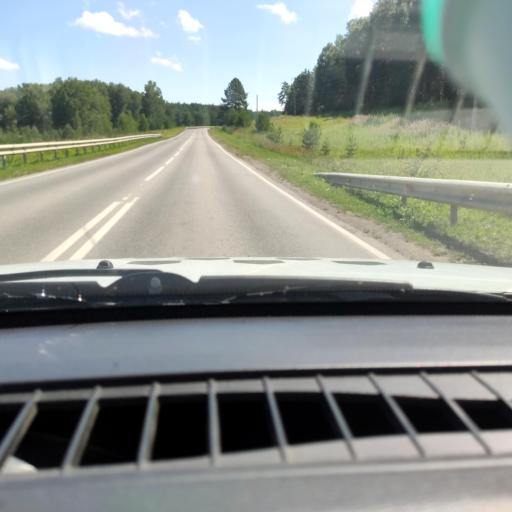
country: RU
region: Bashkortostan
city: Mesyagutovo
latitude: 55.5120
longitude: 58.3130
